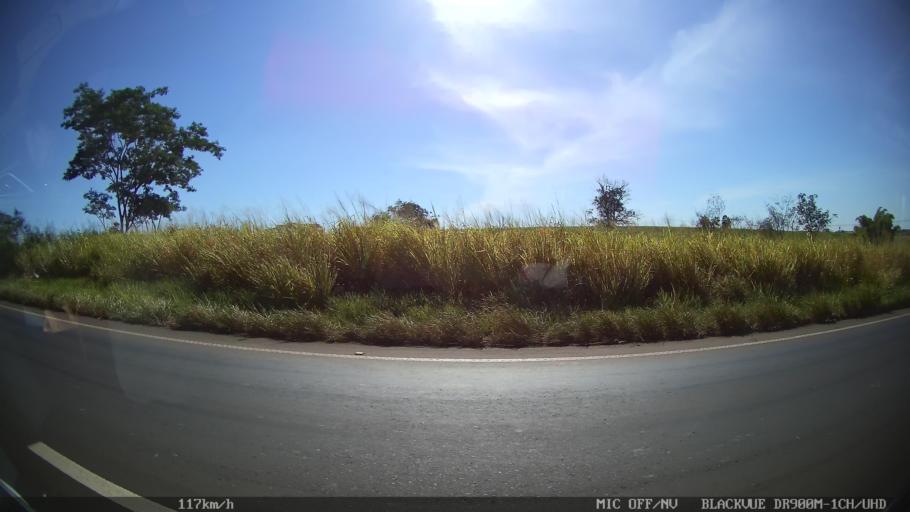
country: BR
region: Sao Paulo
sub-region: Olimpia
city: Olimpia
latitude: -20.6346
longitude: -48.8173
